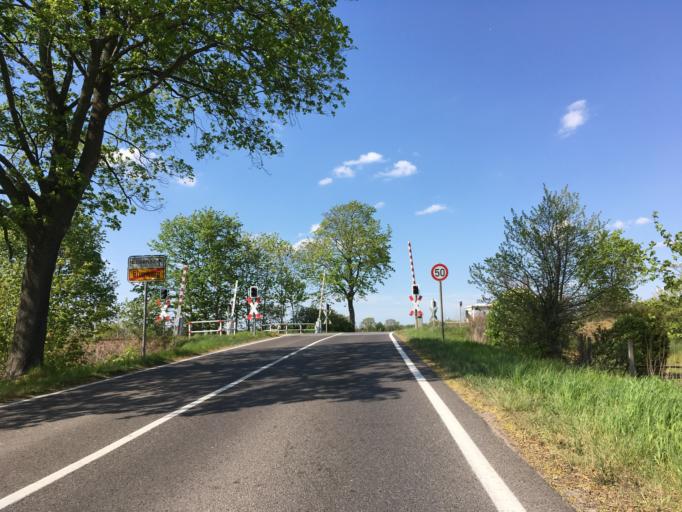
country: DE
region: Brandenburg
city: Ahrensfelde
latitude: 52.6075
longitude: 13.6181
